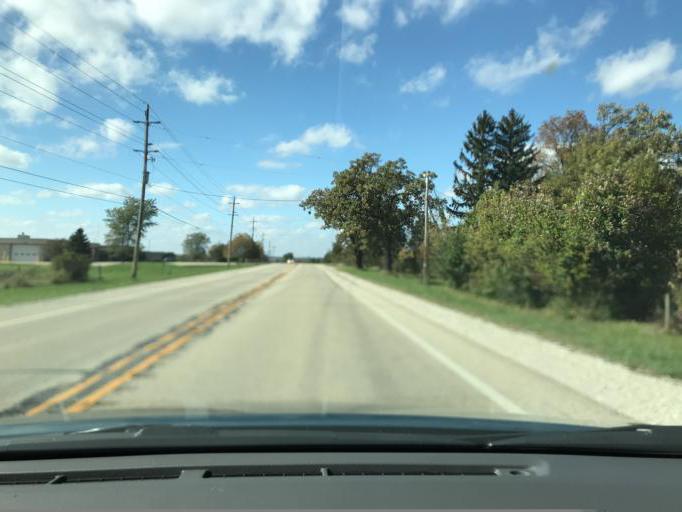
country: US
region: Wisconsin
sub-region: Racine County
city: Union Grove
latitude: 42.6281
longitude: -88.0075
